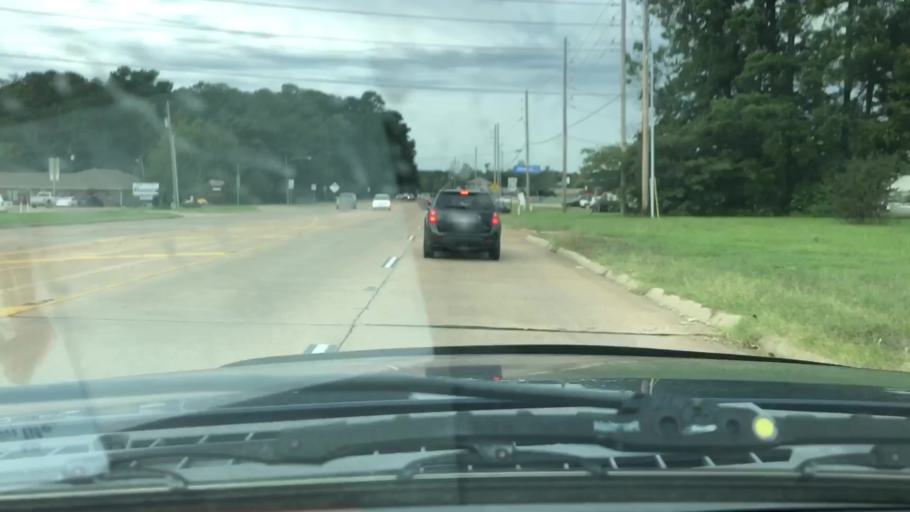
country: US
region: Texas
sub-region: Bowie County
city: Wake Village
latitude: 33.4435
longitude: -94.0984
